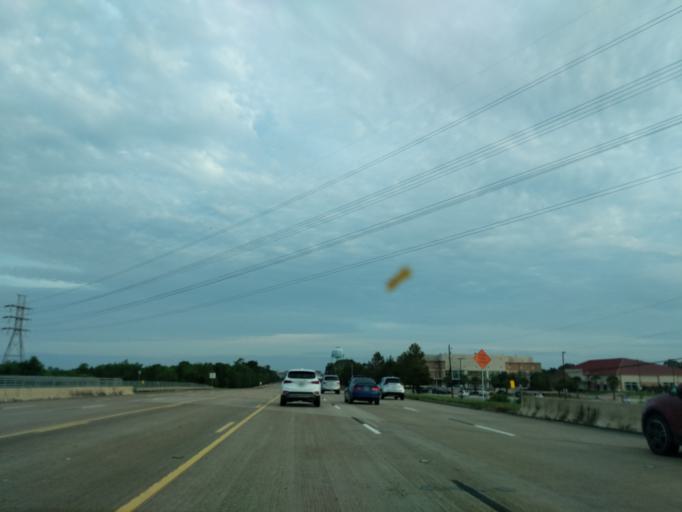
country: US
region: Texas
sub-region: Harris County
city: Nassau Bay
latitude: 29.5284
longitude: -95.0897
